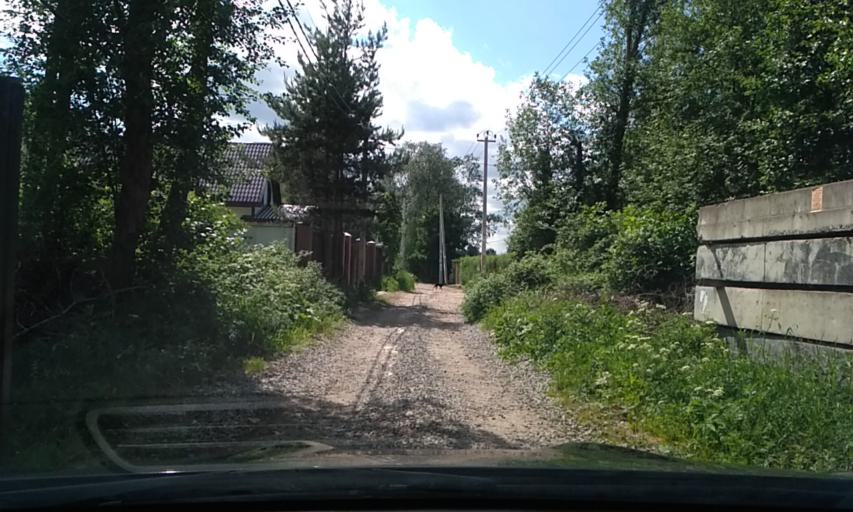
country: RU
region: Leningrad
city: Otradnoye
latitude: 59.8083
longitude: 30.8325
